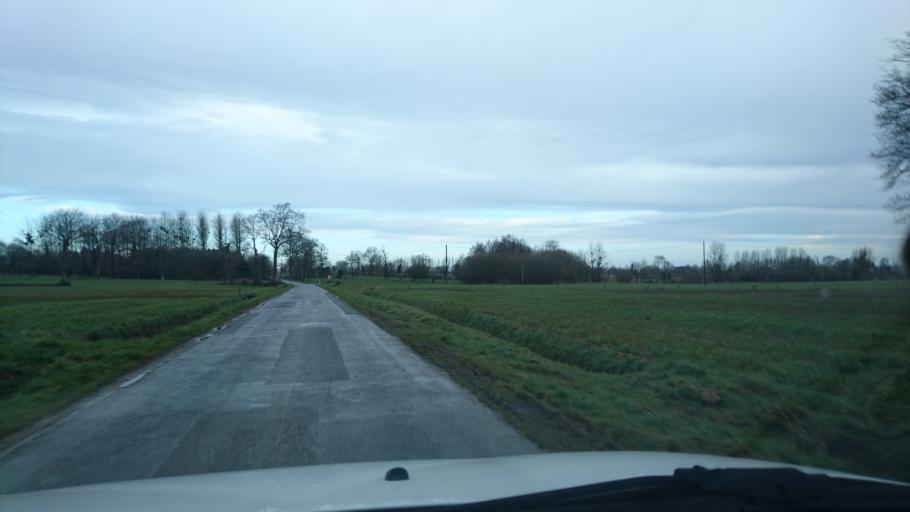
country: FR
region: Brittany
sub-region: Departement d'Ille-et-Vilaine
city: Antrain
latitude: 48.4875
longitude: -1.5192
